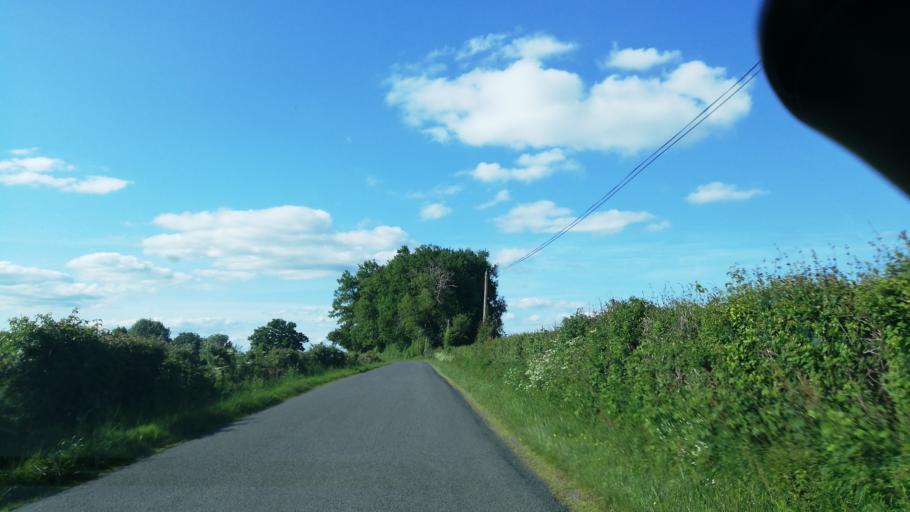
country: FR
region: Poitou-Charentes
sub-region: Departement des Deux-Sevres
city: Moncoutant
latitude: 46.6892
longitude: -0.5722
